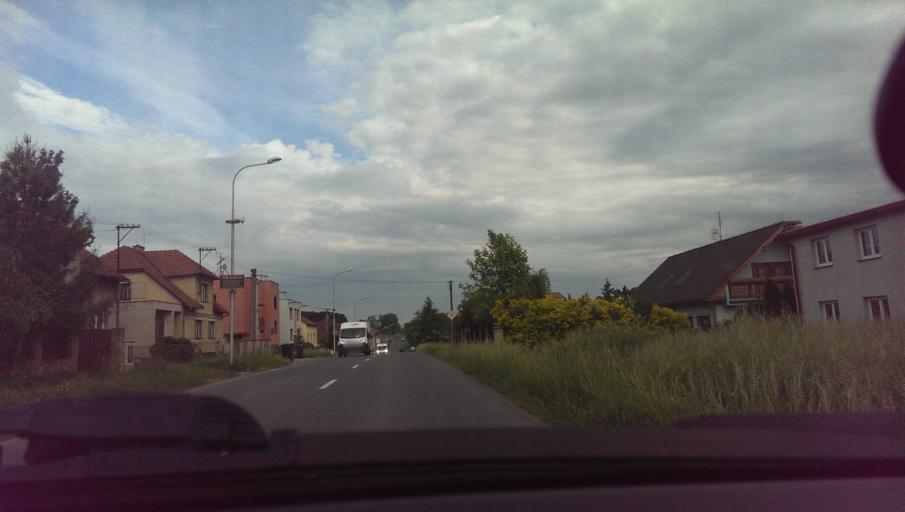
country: CZ
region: Zlin
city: Kvasice
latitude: 49.2670
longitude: 17.4372
